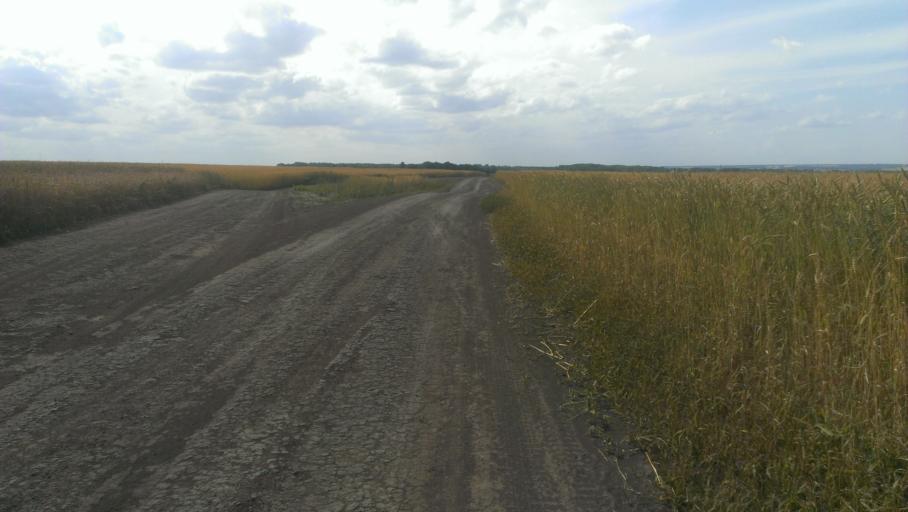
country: RU
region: Altai Krai
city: Gon'ba
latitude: 53.3738
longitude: 83.5487
